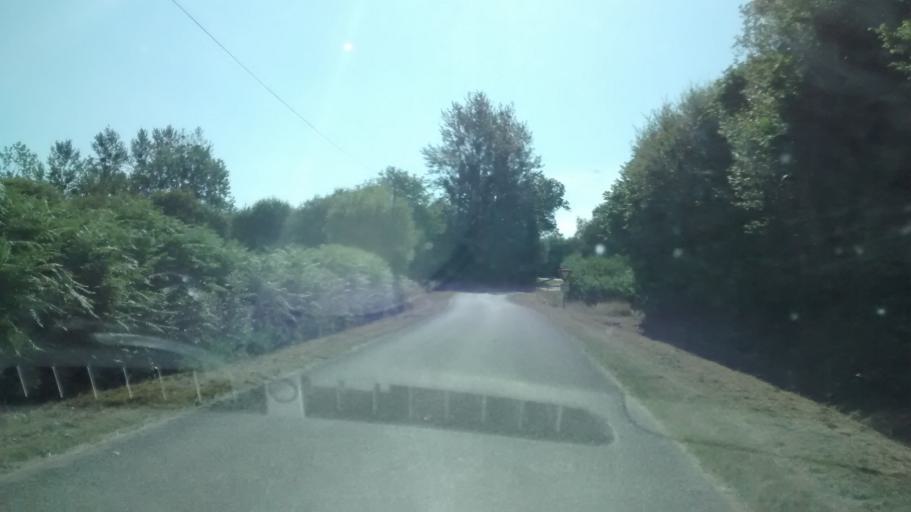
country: FR
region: Brittany
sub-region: Departement du Morbihan
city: Malestroit
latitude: 47.7862
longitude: -2.4273
